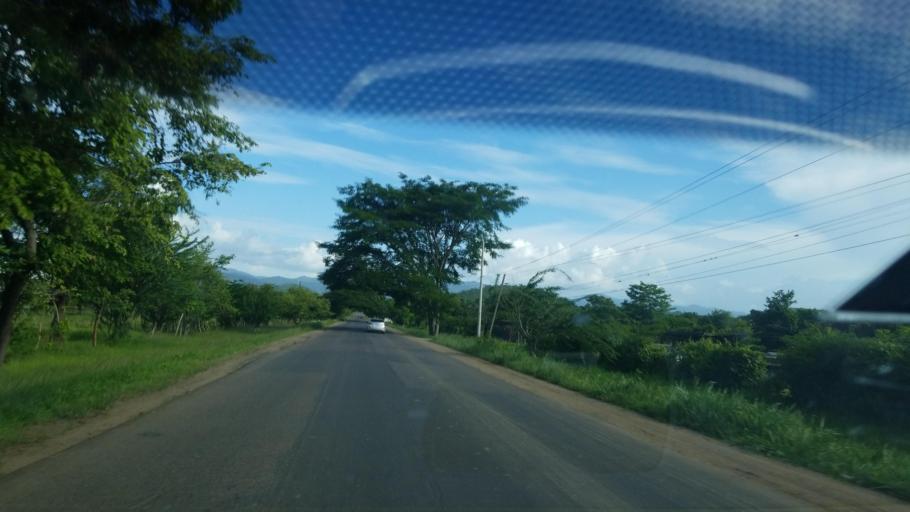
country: HN
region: El Paraiso
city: Arauli
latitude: 13.9553
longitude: -86.5614
